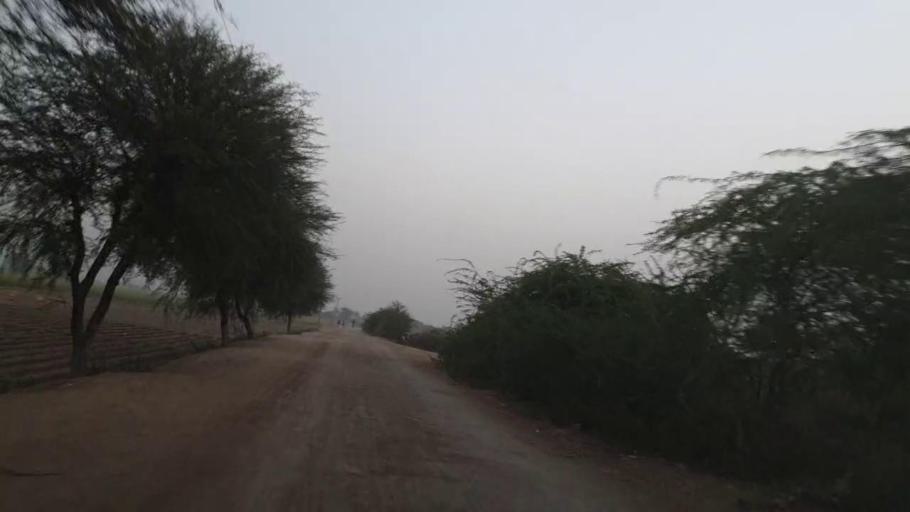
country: PK
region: Sindh
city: Kunri
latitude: 25.1117
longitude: 69.5681
